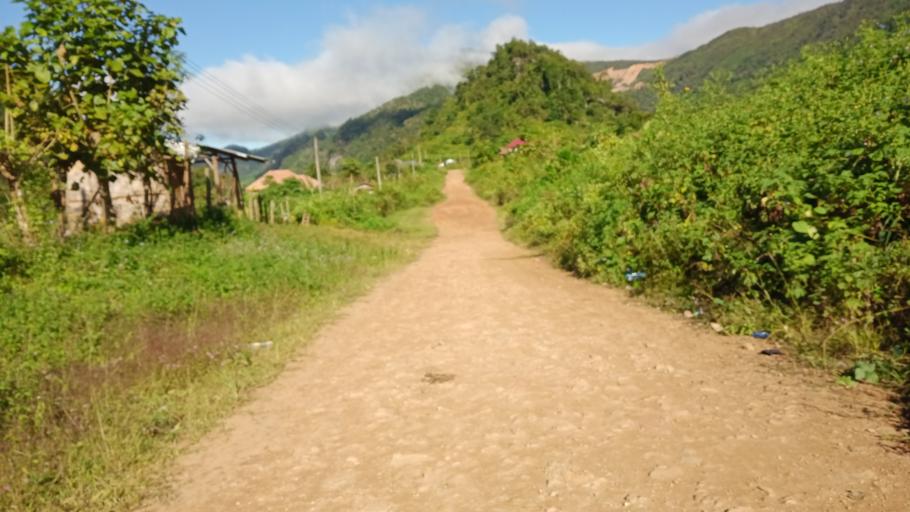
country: LA
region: Xiangkhoang
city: Phonsavan
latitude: 19.1149
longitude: 102.9121
